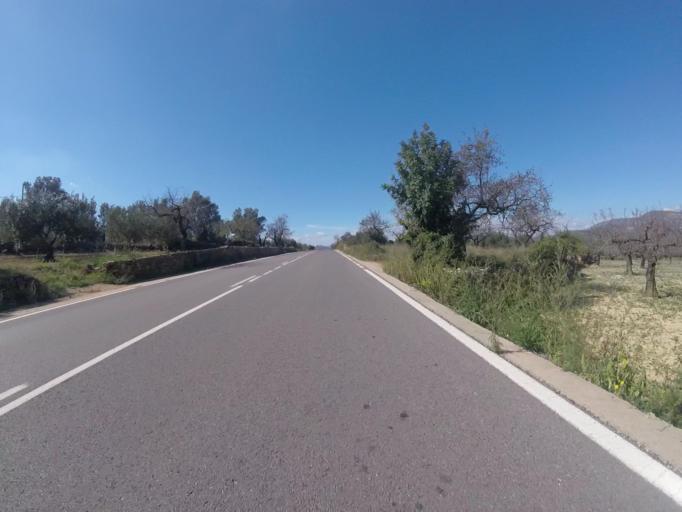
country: ES
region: Valencia
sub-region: Provincia de Castello
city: Albocasser
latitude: 40.3516
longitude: 0.0117
